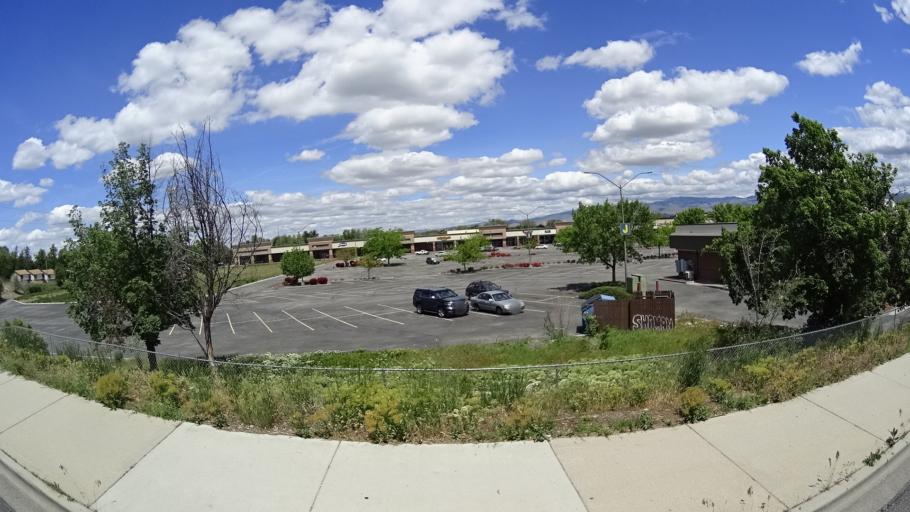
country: US
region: Idaho
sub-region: Ada County
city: Garden City
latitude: 43.5897
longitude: -116.2467
